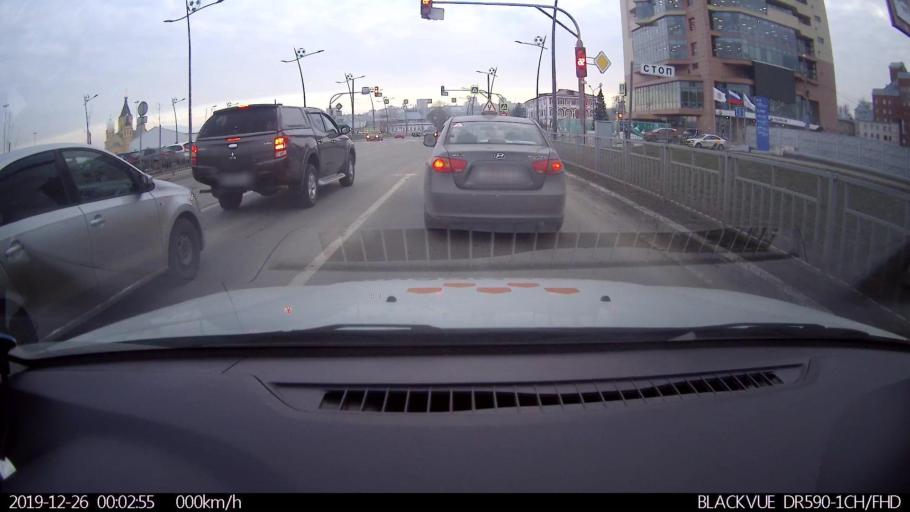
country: RU
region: Nizjnij Novgorod
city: Nizhniy Novgorod
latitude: 56.3336
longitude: 43.9623
